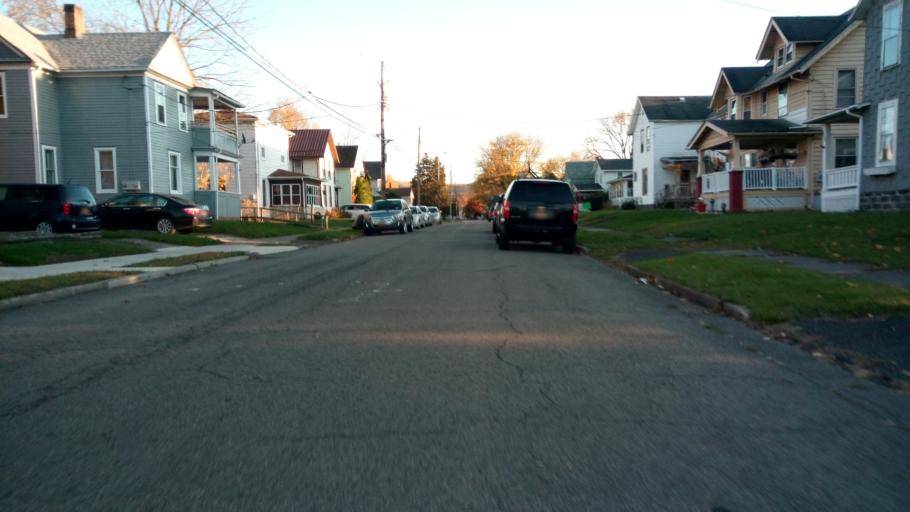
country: US
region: New York
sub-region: Chemung County
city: Elmira
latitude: 42.0769
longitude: -76.8114
